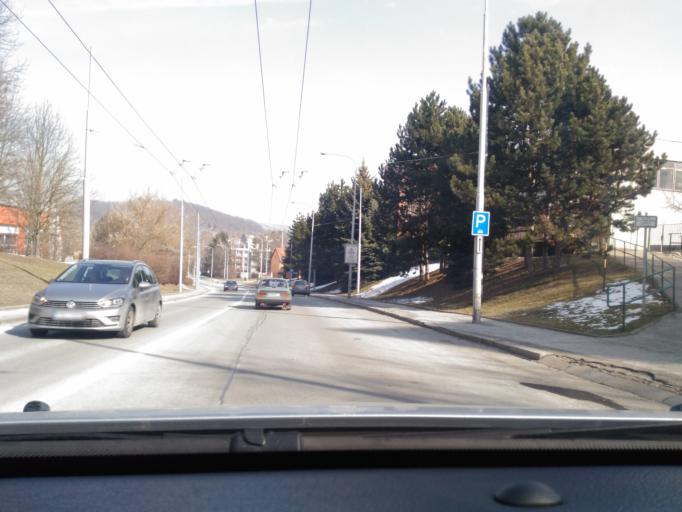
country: CZ
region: South Moravian
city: Troubsko
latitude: 49.2223
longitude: 16.5299
